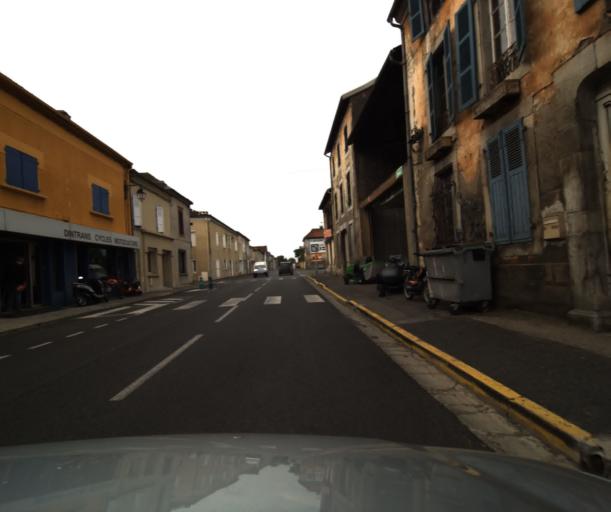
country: FR
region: Midi-Pyrenees
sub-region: Departement des Hautes-Pyrenees
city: Rabastens-de-Bigorre
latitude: 43.3871
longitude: 0.1499
